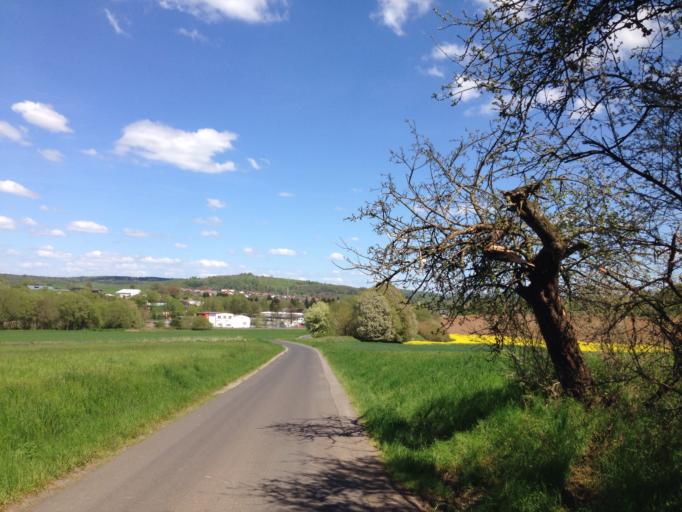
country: DE
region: Hesse
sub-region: Regierungsbezirk Giessen
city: Laubach
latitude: 50.5391
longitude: 8.9630
